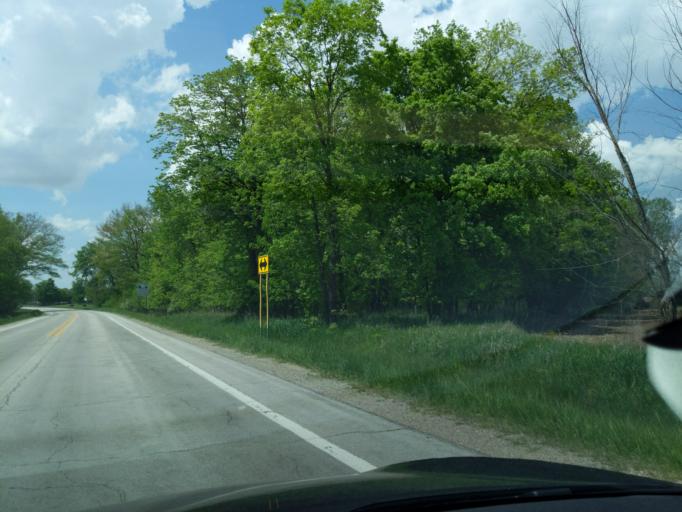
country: US
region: Michigan
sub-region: Ingham County
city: Stockbridge
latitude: 42.5541
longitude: -84.2343
